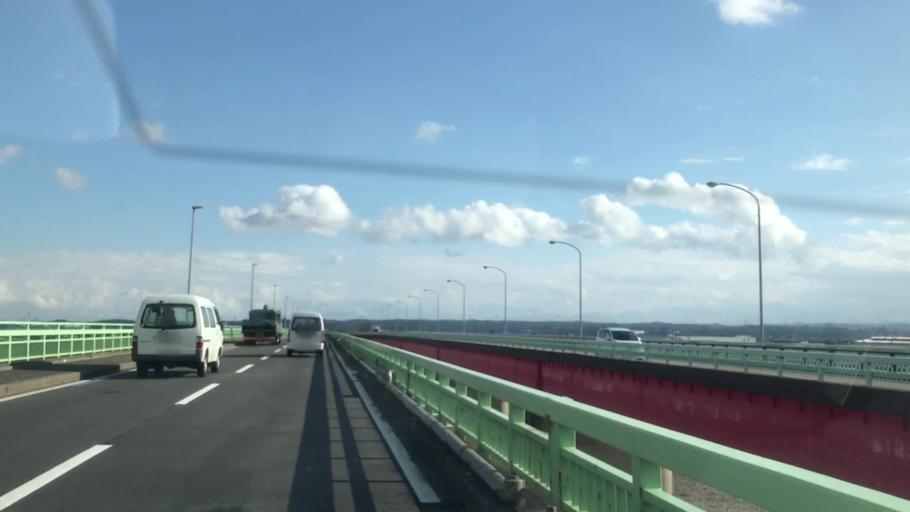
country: JP
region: Toyama
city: Takaoka
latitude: 36.7138
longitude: 137.0223
